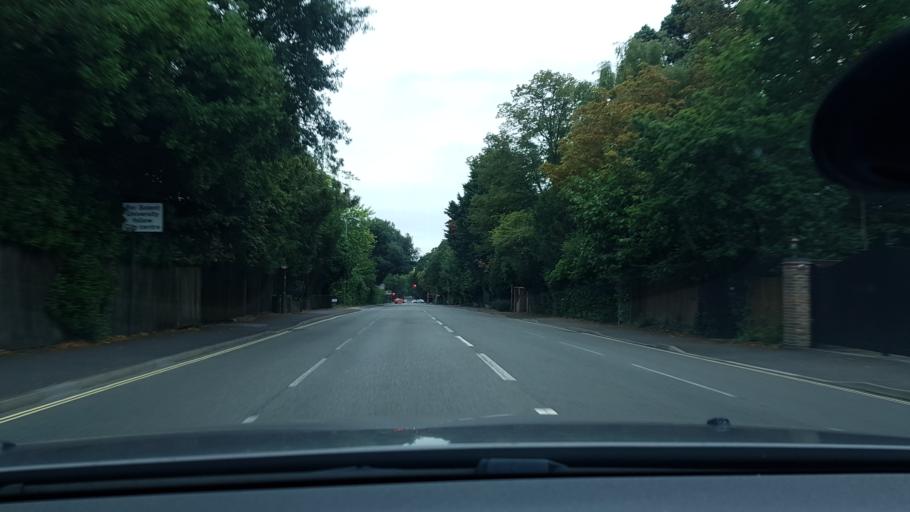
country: GB
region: England
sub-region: Southampton
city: Southampton
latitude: 50.9387
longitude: -1.4067
